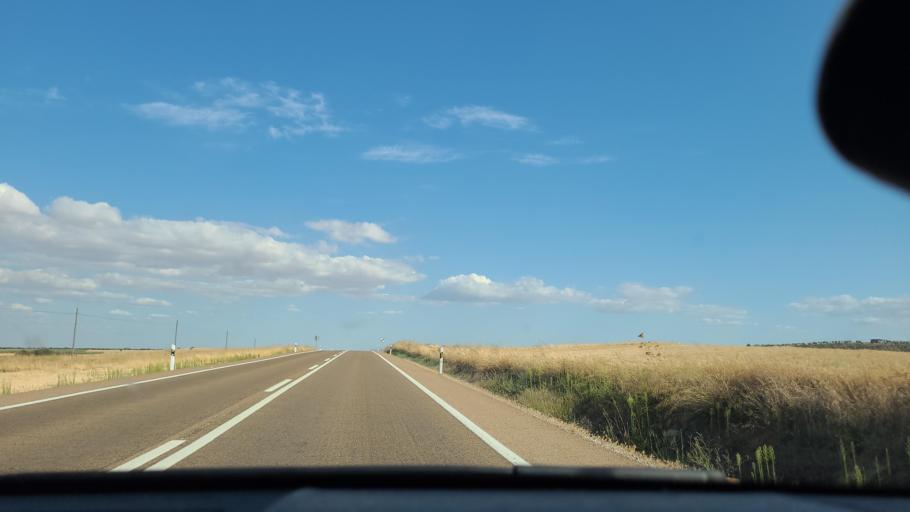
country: ES
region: Extremadura
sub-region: Provincia de Badajoz
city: Usagre
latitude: 38.3303
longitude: -6.1484
